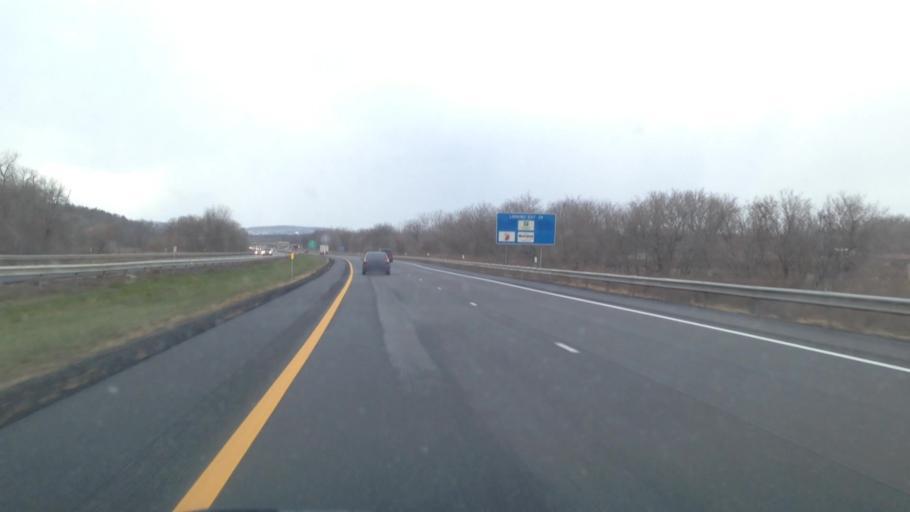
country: US
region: New York
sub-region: Montgomery County
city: Fonda
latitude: 42.9419
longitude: -74.3454
